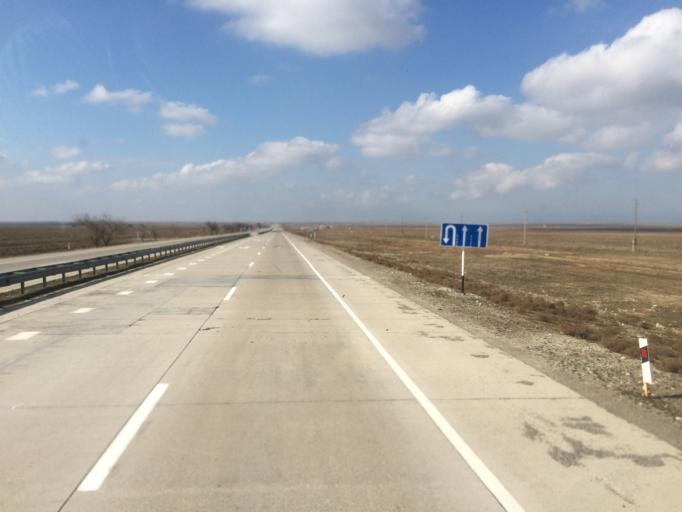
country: KZ
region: Ongtustik Qazaqstan
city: Temirlanovka
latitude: 42.8325
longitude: 69.1234
